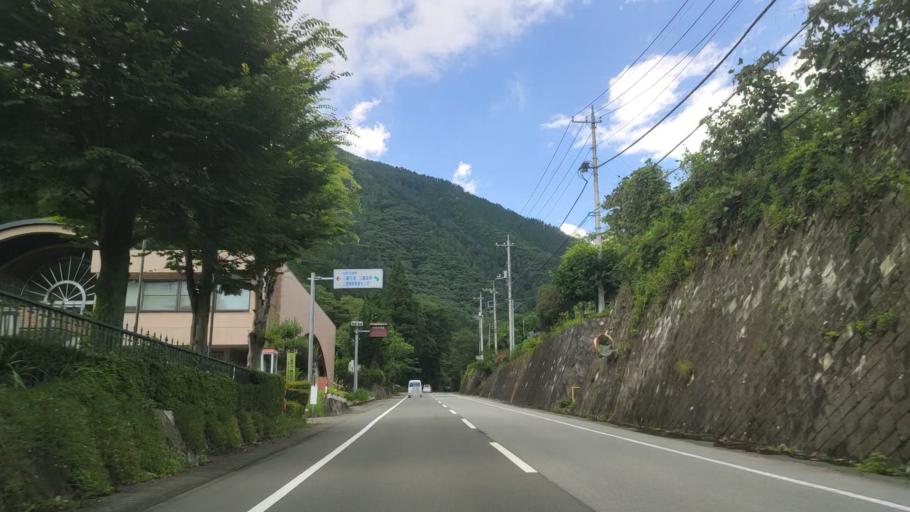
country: JP
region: Yamanashi
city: Enzan
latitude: 35.7930
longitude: 138.7391
